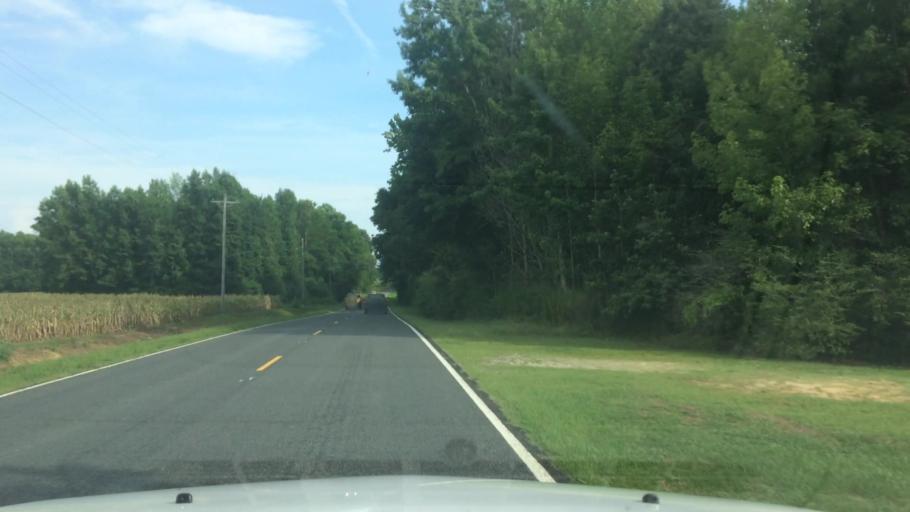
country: US
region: North Carolina
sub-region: Greene County
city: Maury
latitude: 35.4974
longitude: -77.5228
